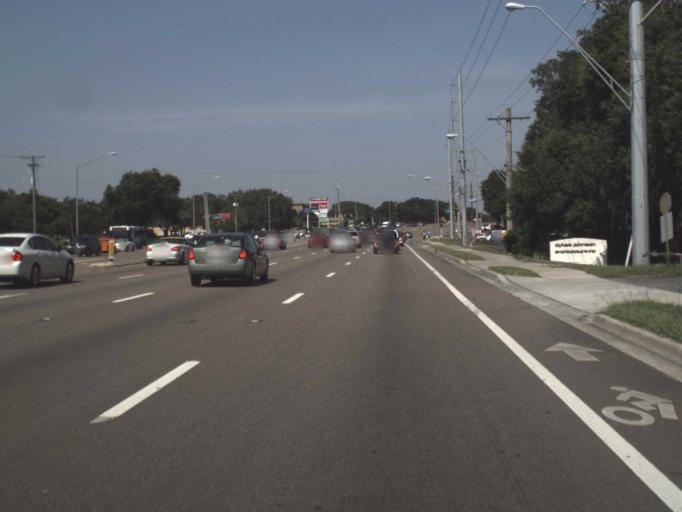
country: US
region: Florida
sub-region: Hillsborough County
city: Brandon
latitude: 27.9378
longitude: -82.3163
